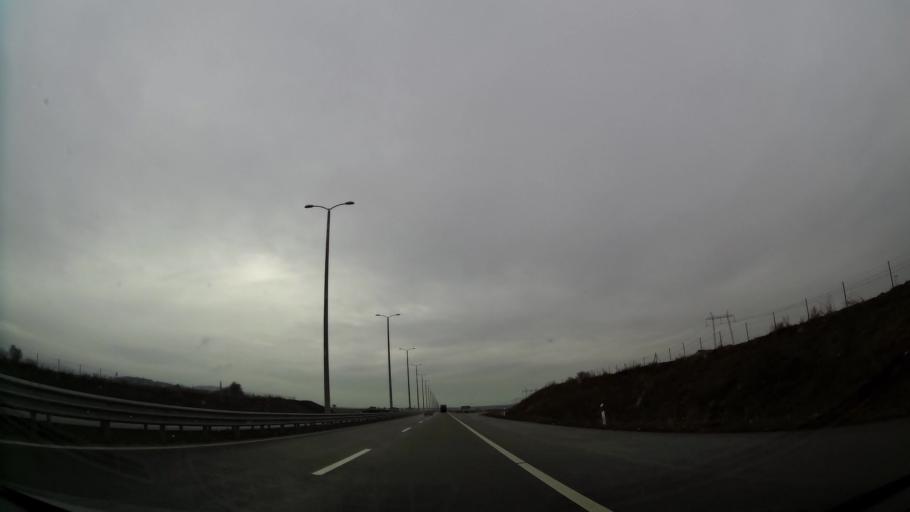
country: XK
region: Pristina
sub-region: Lipjan
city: Lipljan
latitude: 42.4983
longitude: 21.1867
